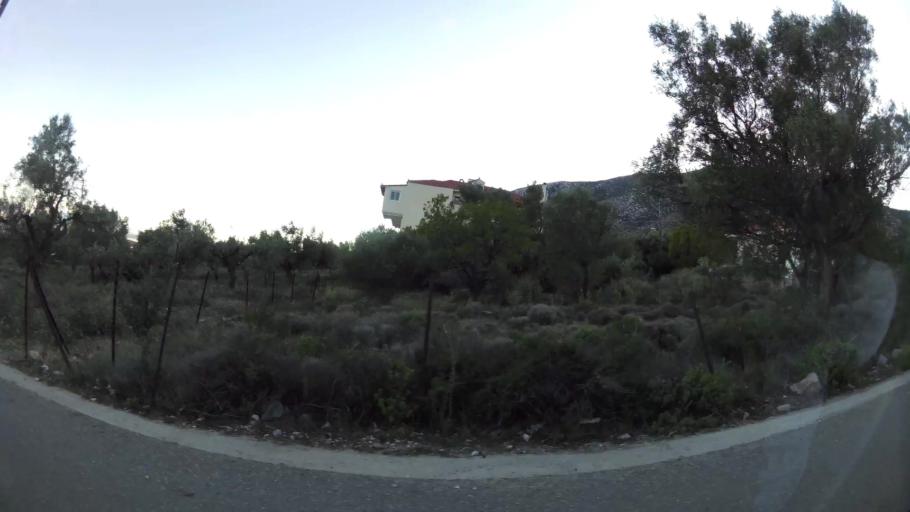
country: GR
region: Attica
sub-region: Nomarchia Anatolikis Attikis
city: Leondarion
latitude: 37.9720
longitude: 23.8379
